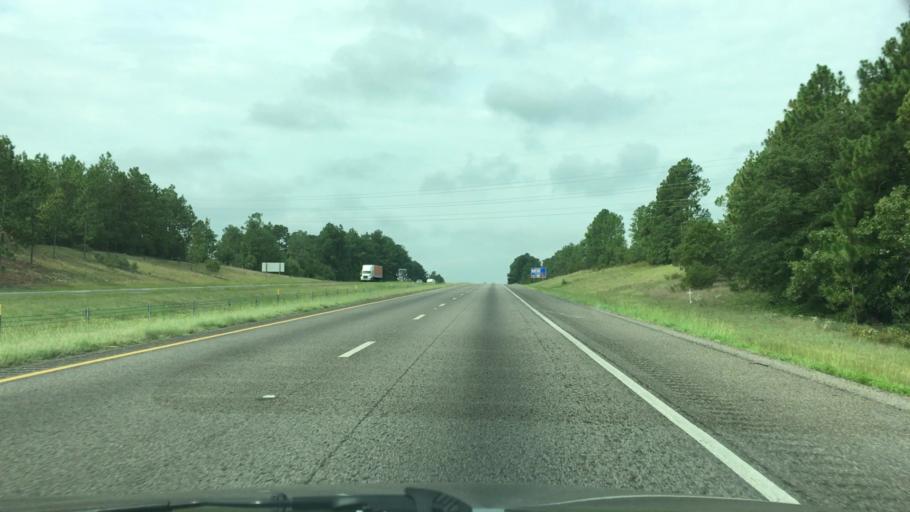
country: US
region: South Carolina
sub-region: Aiken County
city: Graniteville
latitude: 33.6163
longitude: -81.8303
